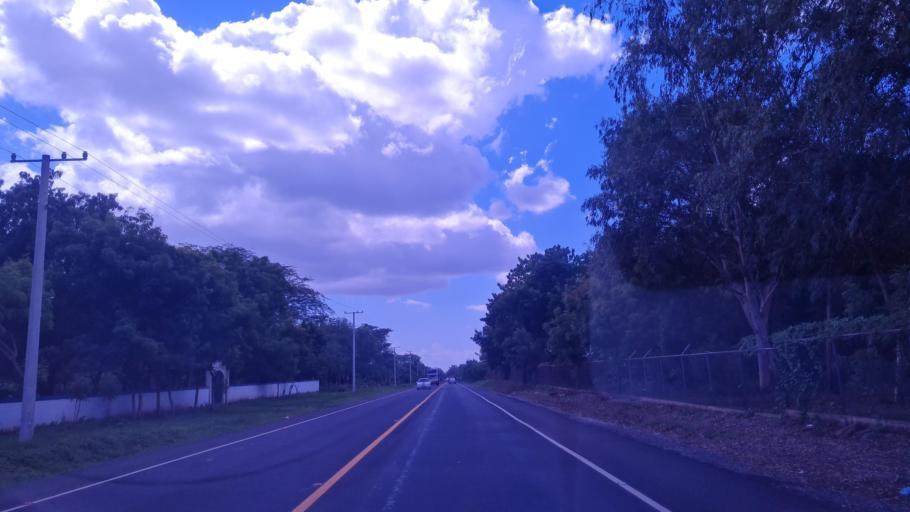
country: NI
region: Masaya
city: Nindiri
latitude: 12.0296
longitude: -86.1236
